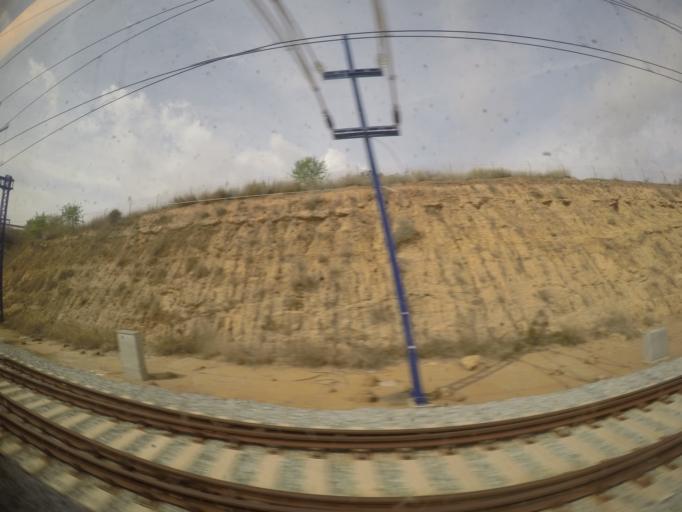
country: ES
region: Catalonia
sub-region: Provincia de Tarragona
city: Santa Oliva
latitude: 41.2488
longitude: 1.5705
